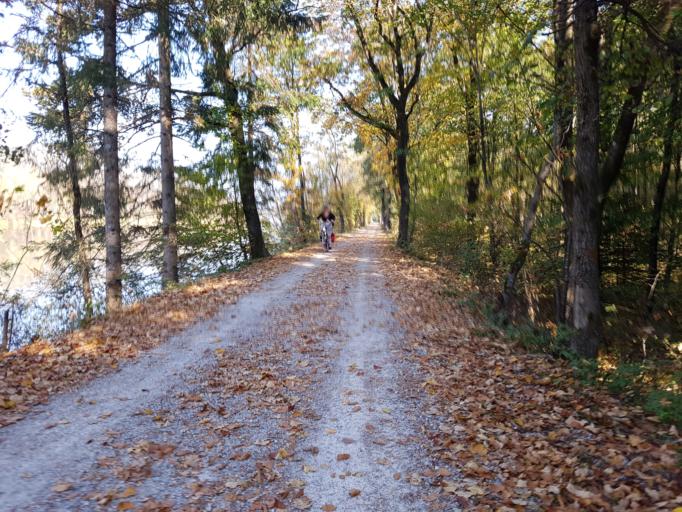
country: AT
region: Salzburg
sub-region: Politischer Bezirk Hallein
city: Puch bei Hallein
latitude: 47.7142
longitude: 13.0815
